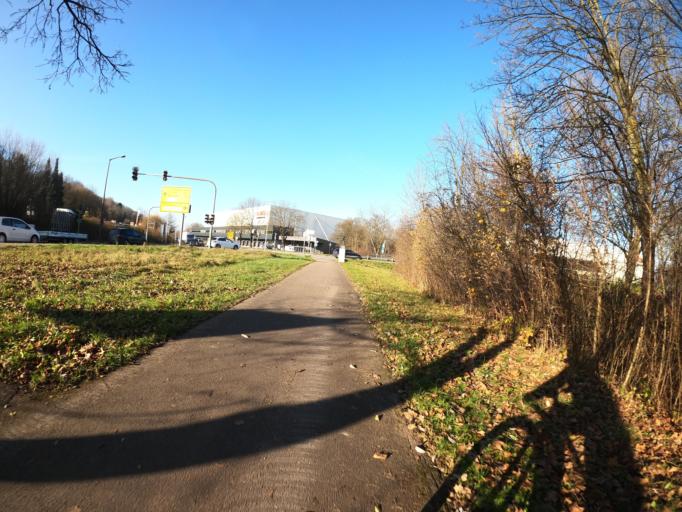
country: DE
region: Baden-Wuerttemberg
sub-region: Regierungsbezirk Stuttgart
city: Goeppingen
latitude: 48.6899
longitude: 9.6710
